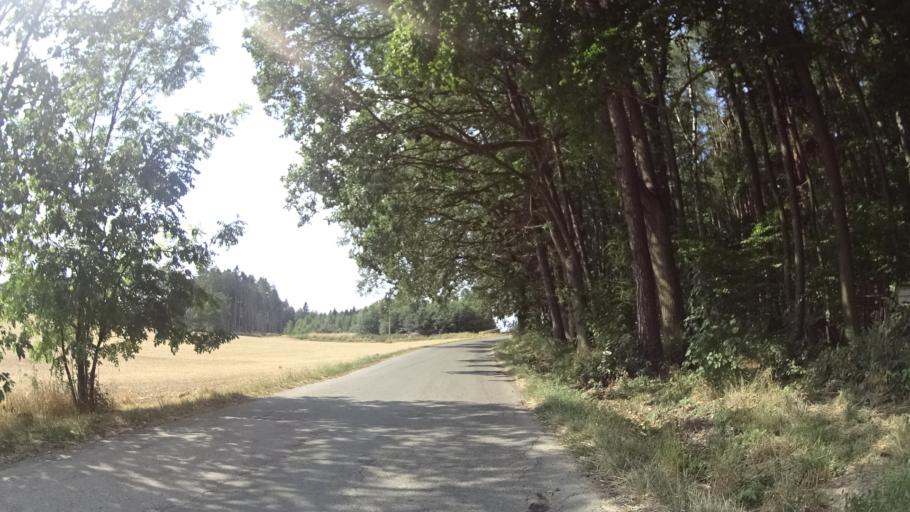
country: CZ
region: Kralovehradecky
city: Liban
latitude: 50.4279
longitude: 15.2587
